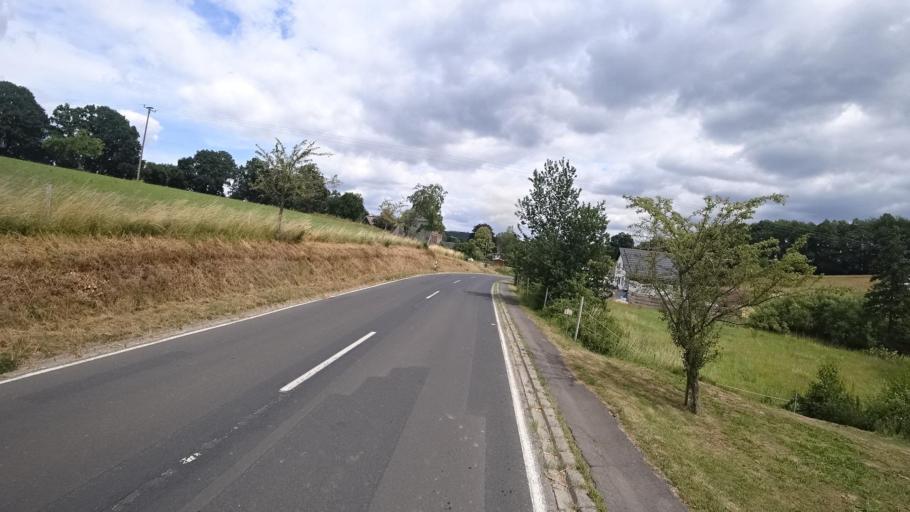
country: DE
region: Rheinland-Pfalz
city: Oberirsen
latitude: 50.7225
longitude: 7.5784
